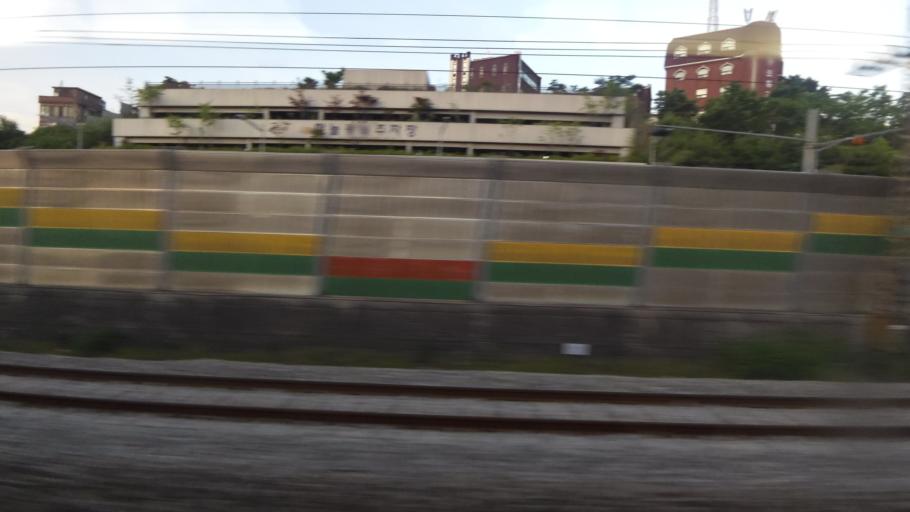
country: KR
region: Gyeonggi-do
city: Kwangmyong
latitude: 37.4869
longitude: 126.8803
